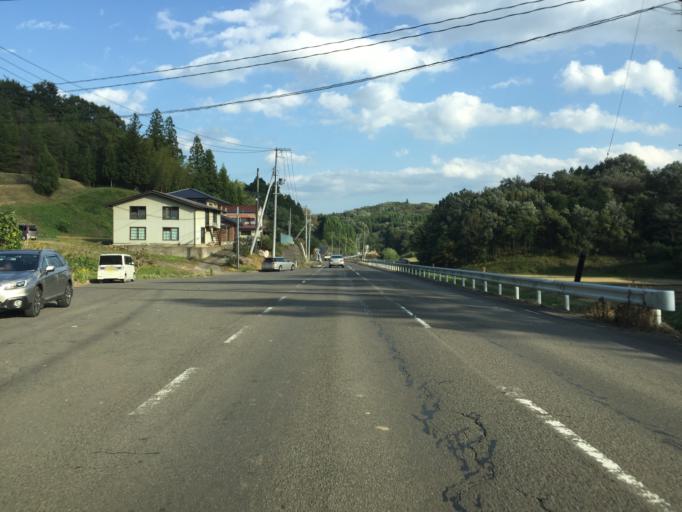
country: JP
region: Fukushima
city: Fukushima-shi
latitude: 37.6835
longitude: 140.4813
